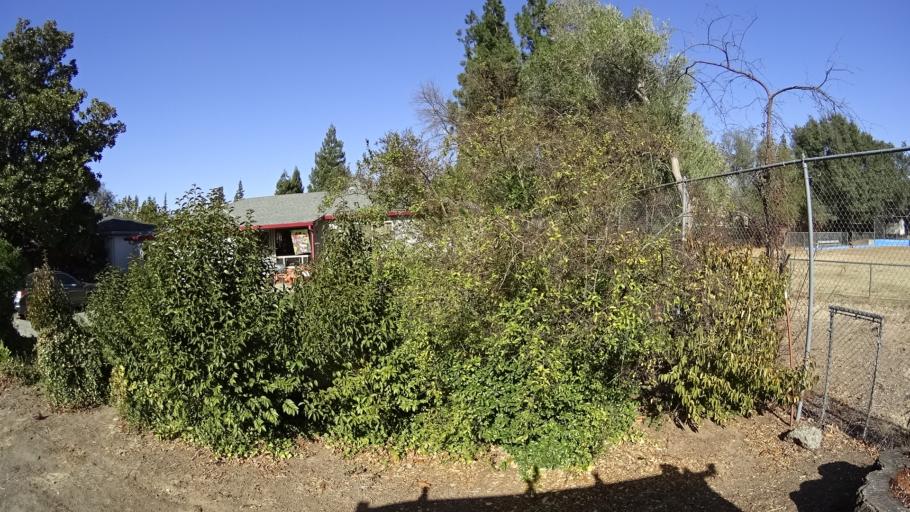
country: US
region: California
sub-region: Sacramento County
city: Citrus Heights
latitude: 38.7045
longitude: -121.2759
